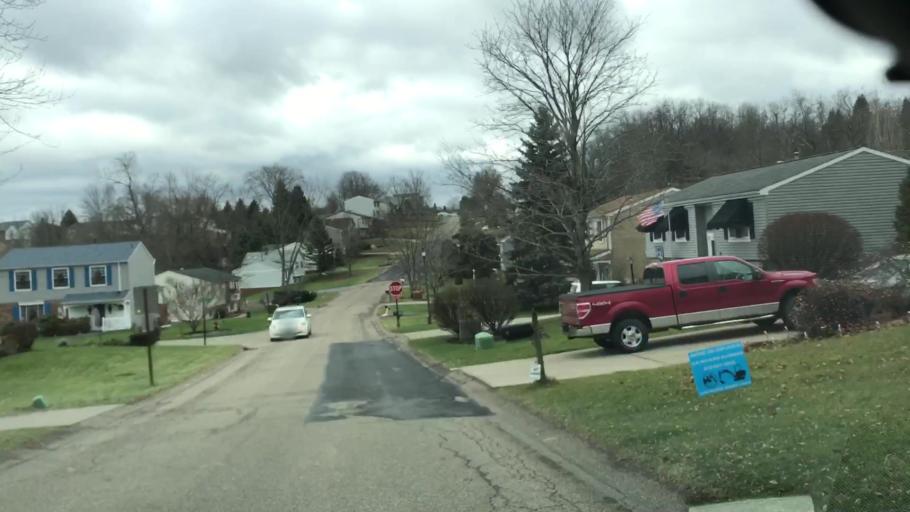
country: US
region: Pennsylvania
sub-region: Allegheny County
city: Enlow
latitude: 40.4485
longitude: -80.2254
